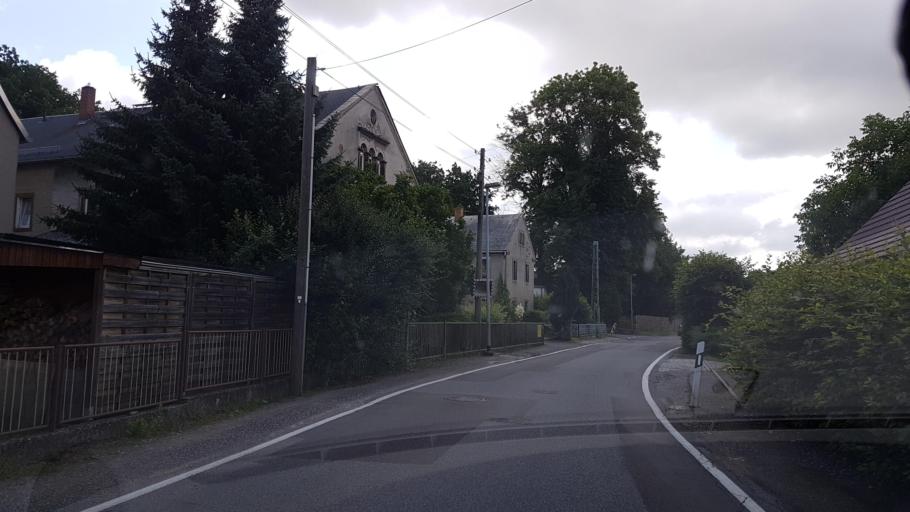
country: DE
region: Saxony
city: Wachau
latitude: 51.1900
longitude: 13.9008
